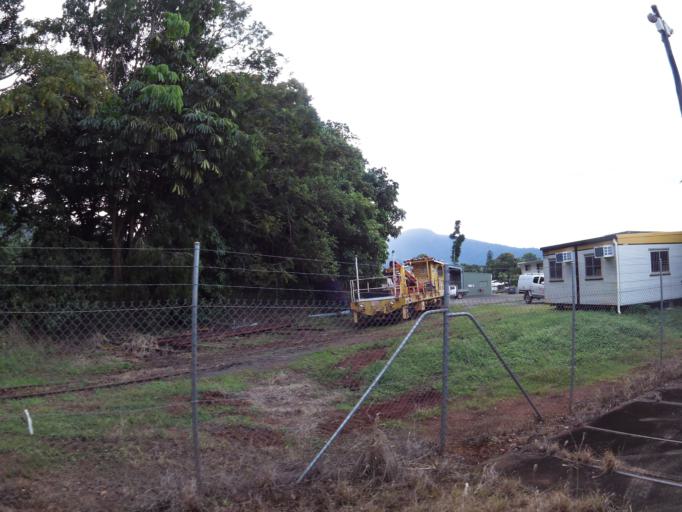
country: AU
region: Queensland
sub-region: Cairns
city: Redlynch
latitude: -16.8883
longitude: 145.6953
